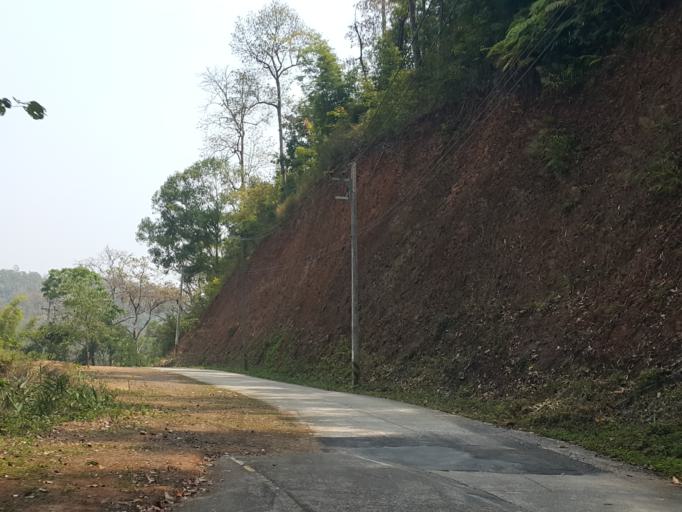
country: TH
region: Lampang
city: Mueang Pan
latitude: 18.8199
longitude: 99.4313
